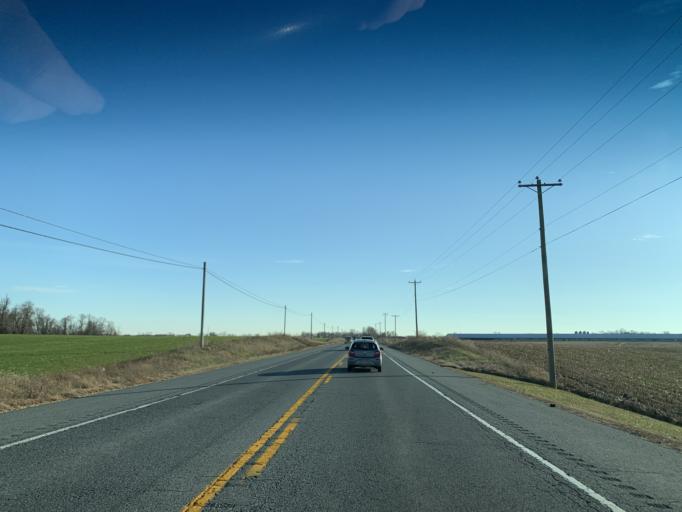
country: US
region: Delaware
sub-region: New Castle County
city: Middletown
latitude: 39.4533
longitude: -75.8701
